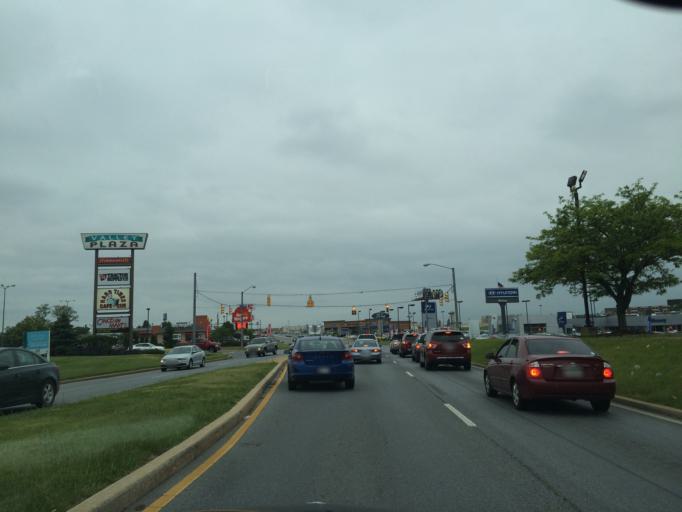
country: US
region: Maryland
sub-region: Washington County
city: Halfway
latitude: 39.6296
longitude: -77.7641
